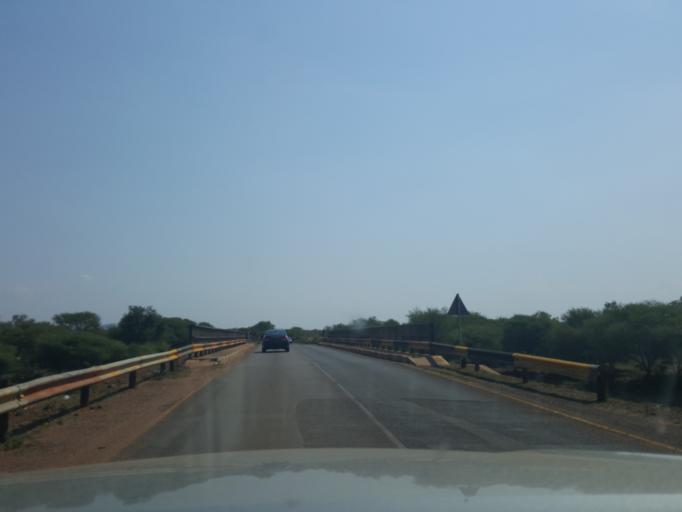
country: BW
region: South East
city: Ramotswa
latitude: -24.8496
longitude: 25.8302
